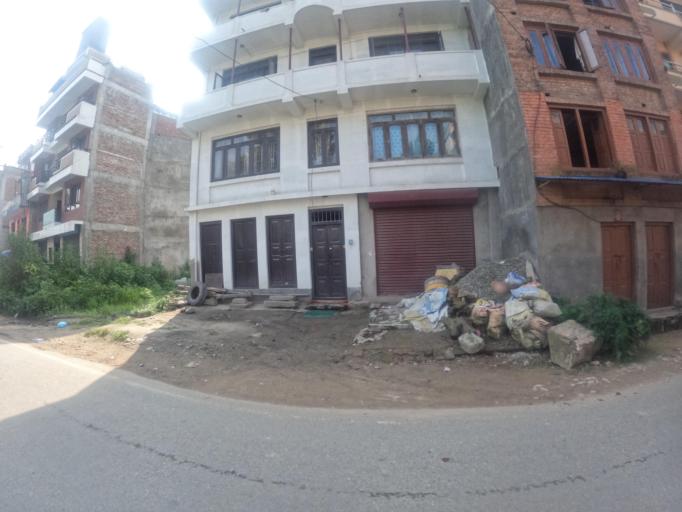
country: NP
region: Central Region
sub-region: Bagmati Zone
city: Bhaktapur
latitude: 27.6798
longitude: 85.4355
